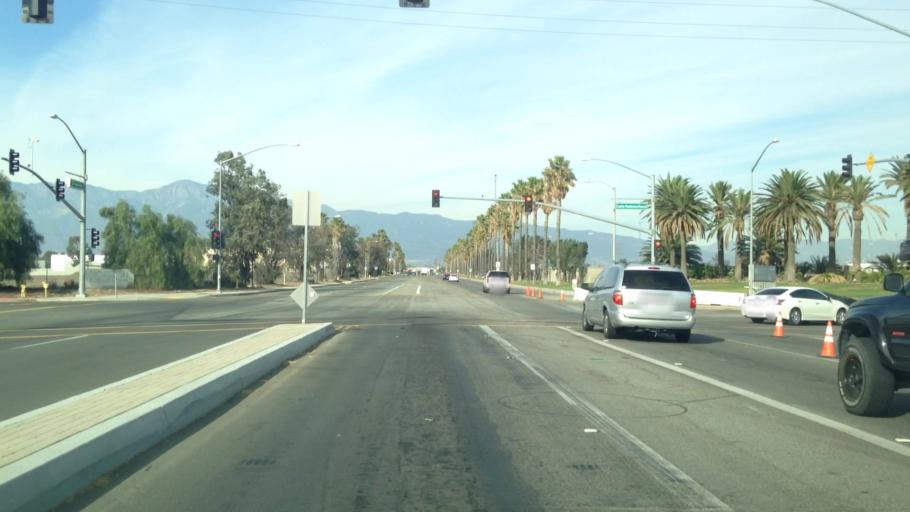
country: US
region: California
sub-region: Riverside County
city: Mira Loma
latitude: 34.0037
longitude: -117.5245
